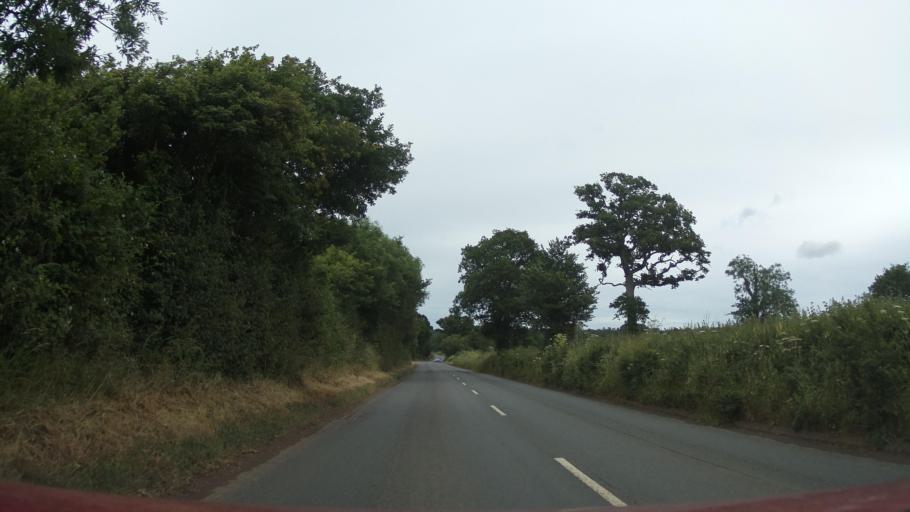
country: GB
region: England
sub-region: Devon
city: Newton Poppleford
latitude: 50.7531
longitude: -3.3681
